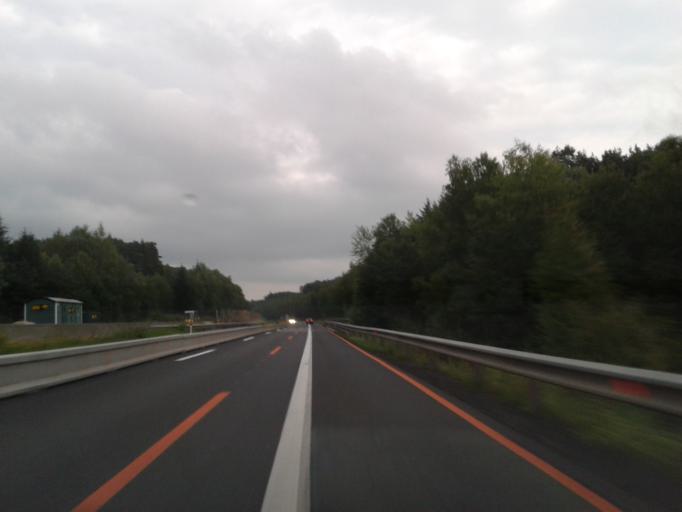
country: AT
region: Styria
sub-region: Politischer Bezirk Hartberg-Fuerstenfeld
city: Bad Waltersdorf
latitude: 47.1474
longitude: 15.9952
